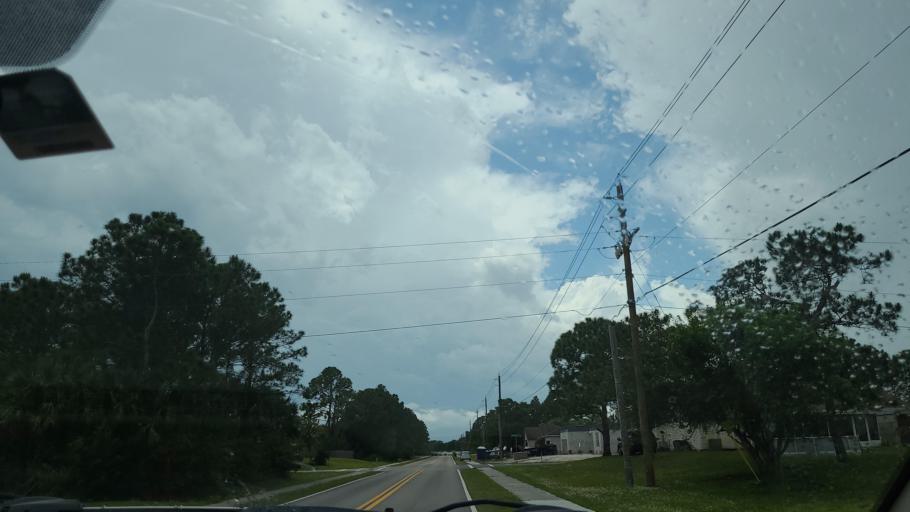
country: US
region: Florida
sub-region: Brevard County
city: Grant-Valkaria
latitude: 27.9482
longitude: -80.6415
